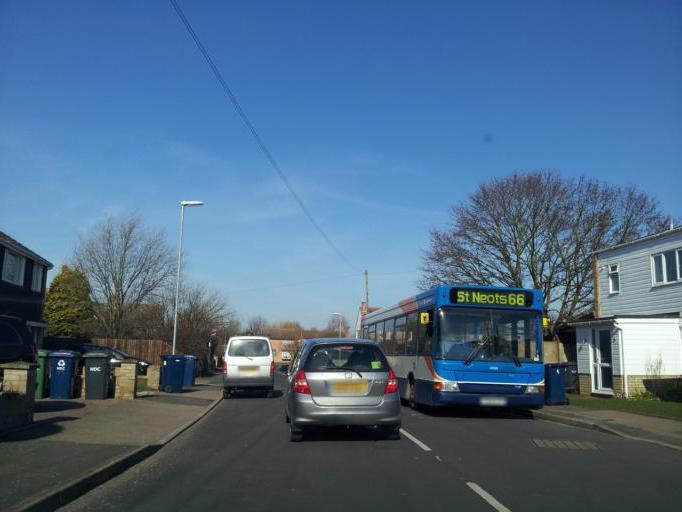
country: GB
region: England
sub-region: Cambridgeshire
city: Little Paxton
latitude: 52.2495
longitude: -0.2584
